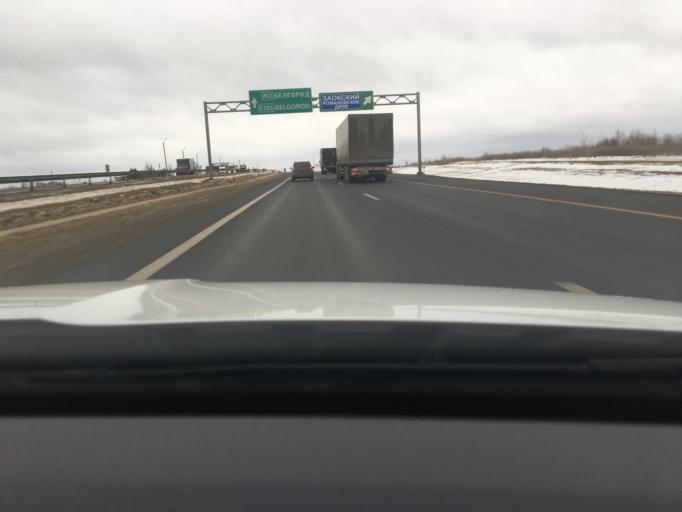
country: RU
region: Moskovskaya
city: Serpukhov
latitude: 54.8428
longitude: 37.4641
